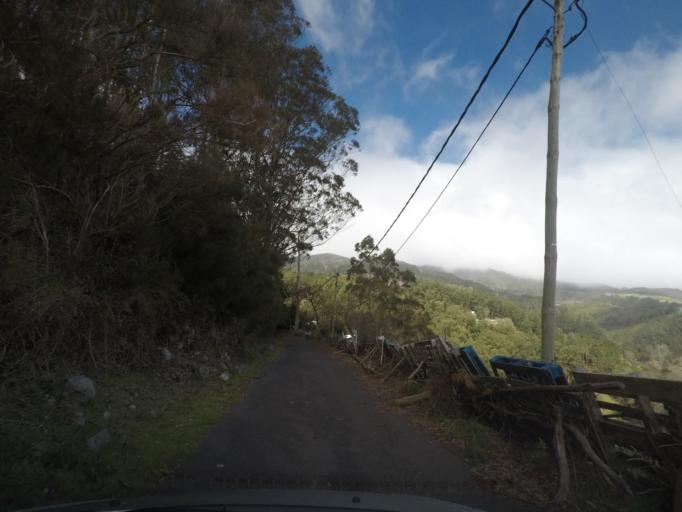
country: PT
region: Madeira
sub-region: Santa Cruz
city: Camacha
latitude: 32.6908
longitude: -16.8742
